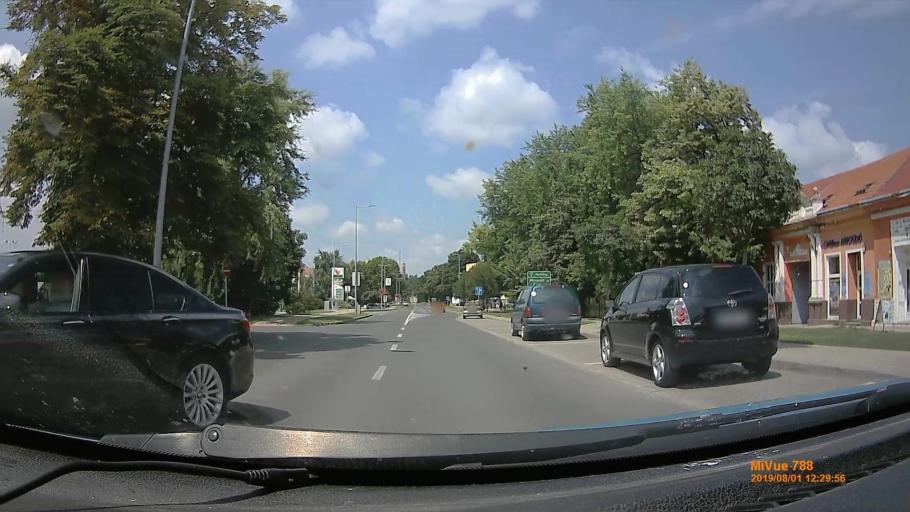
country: HU
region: Baranya
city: Siklos
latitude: 45.8566
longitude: 18.2937
